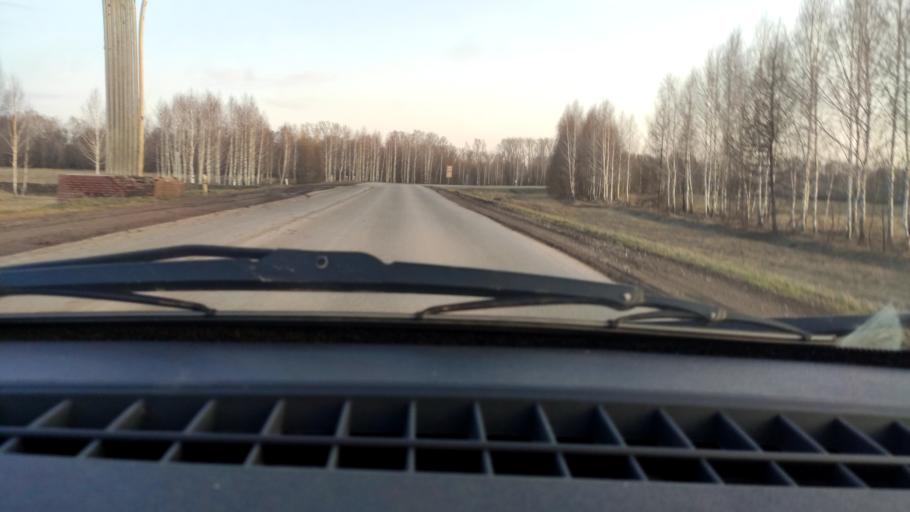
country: RU
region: Bashkortostan
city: Davlekanovo
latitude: 54.3648
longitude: 55.1956
